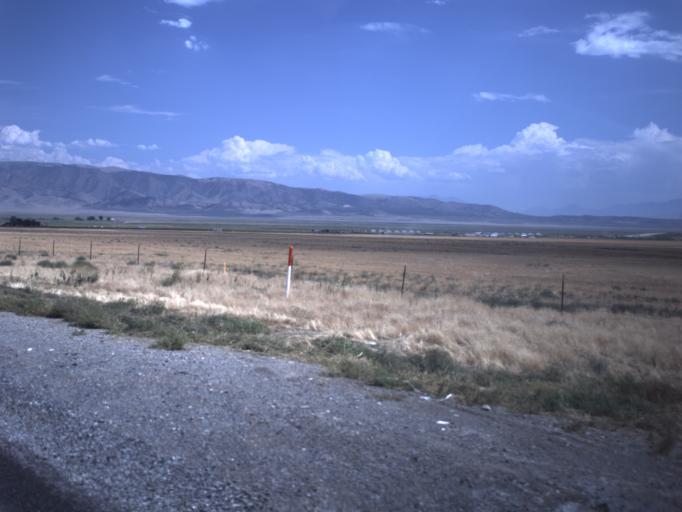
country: US
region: Utah
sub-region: Utah County
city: Eagle Mountain
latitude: 40.2506
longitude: -112.1204
